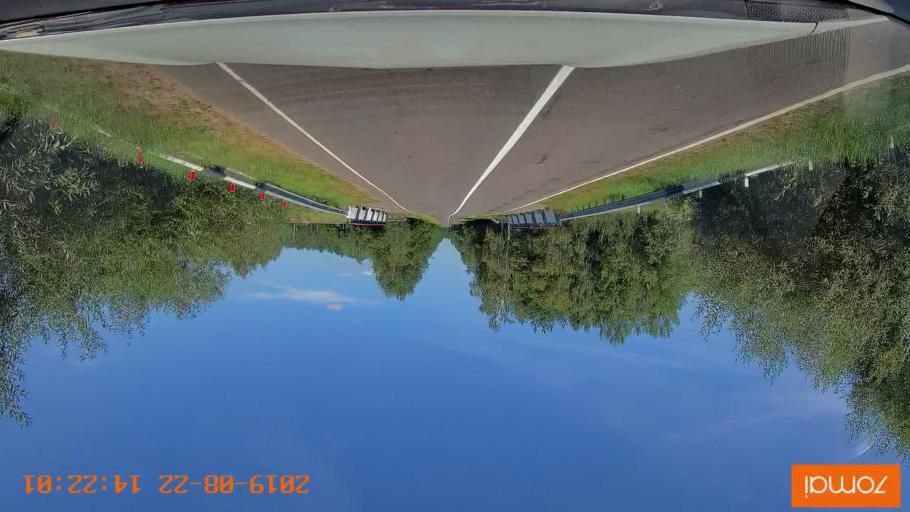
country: BY
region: Mogilev
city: Asipovichy
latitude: 53.2712
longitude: 28.5677
